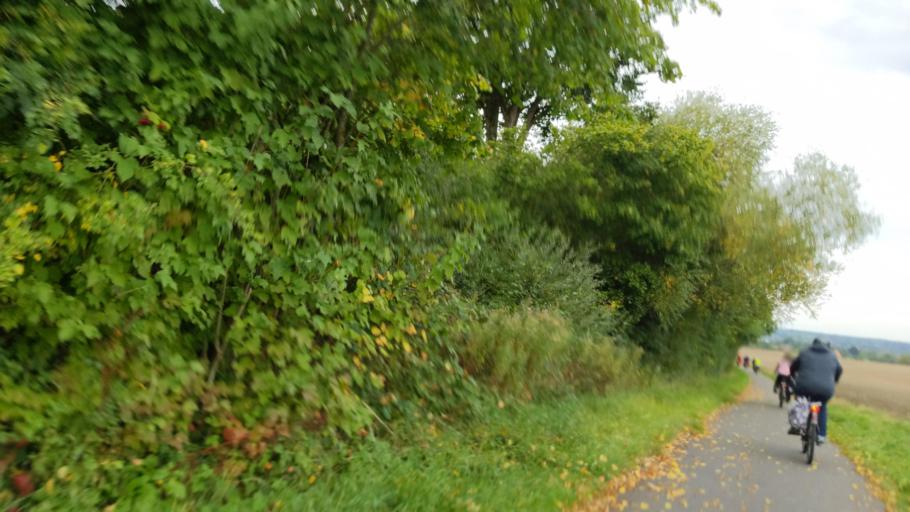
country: DE
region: Schleswig-Holstein
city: Buchholz
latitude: 53.7635
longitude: 10.7841
